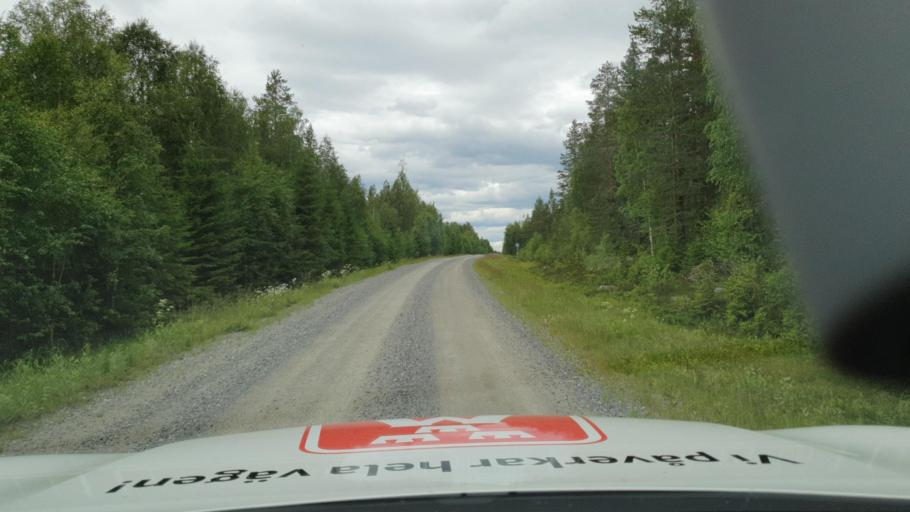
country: SE
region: Vaesterbotten
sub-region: Nordmalings Kommun
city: Nordmaling
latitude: 63.7403
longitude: 19.3883
